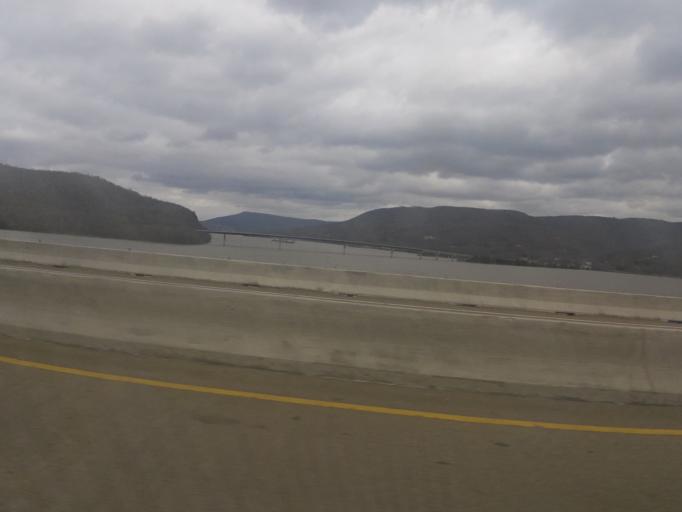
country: US
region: Tennessee
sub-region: Marion County
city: Jasper
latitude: 35.0216
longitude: -85.5509
